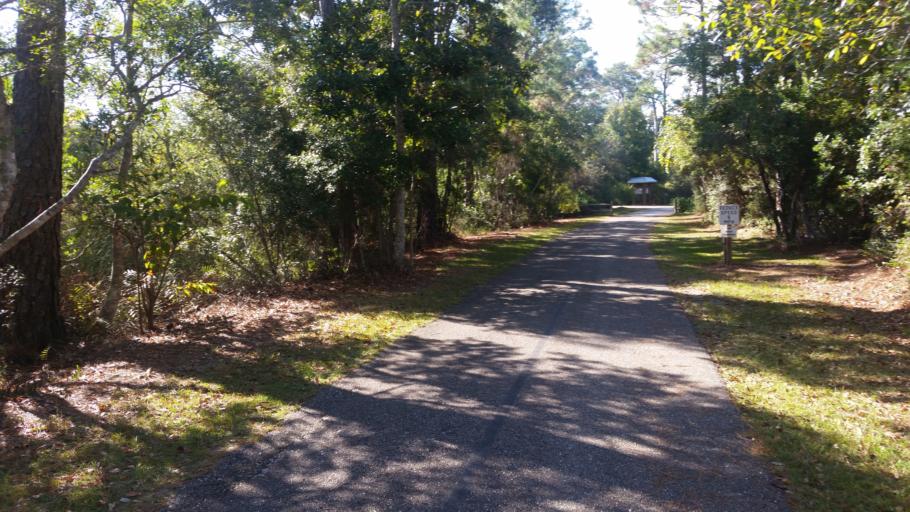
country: US
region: Alabama
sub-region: Baldwin County
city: Orange Beach
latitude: 30.2747
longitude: -87.6060
